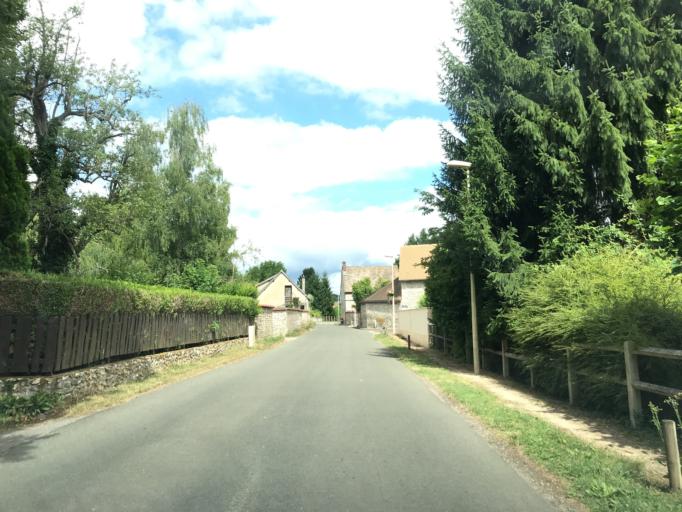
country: FR
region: Haute-Normandie
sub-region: Departement de l'Eure
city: Houlbec-Cocherel
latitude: 49.0634
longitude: 1.2951
